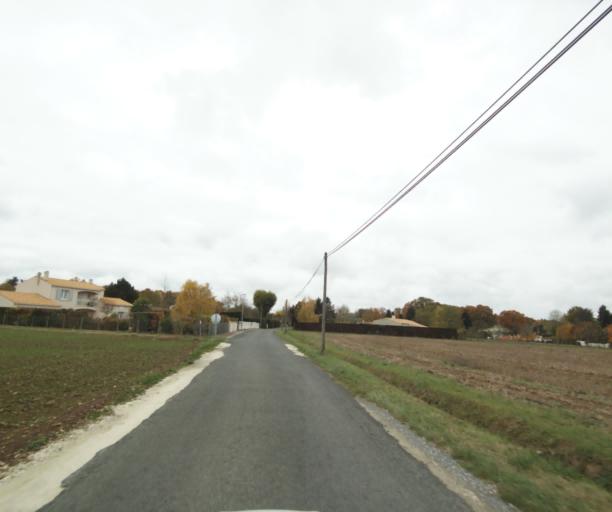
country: FR
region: Poitou-Charentes
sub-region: Departement de la Charente-Maritime
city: Saintes
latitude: 45.7656
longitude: -0.6387
